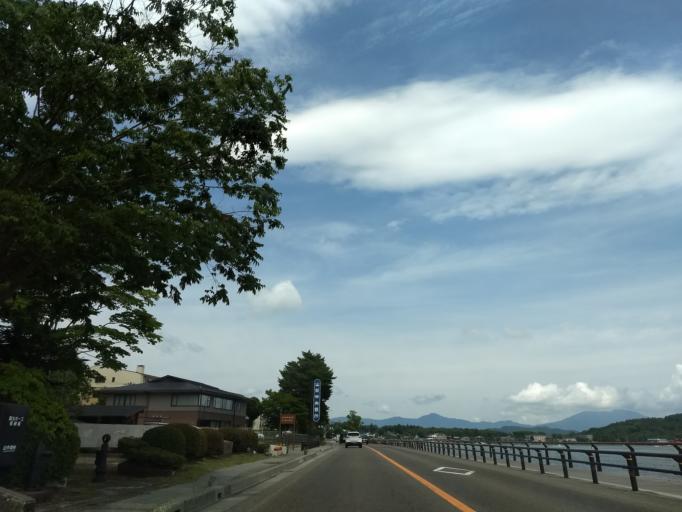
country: JP
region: Shizuoka
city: Gotemba
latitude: 35.4191
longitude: 138.8547
